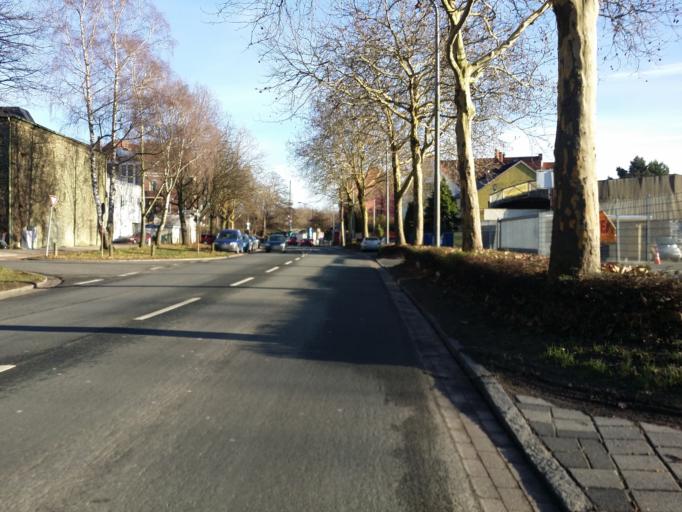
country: DE
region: Bremen
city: Bremen
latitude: 53.0757
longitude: 8.7817
